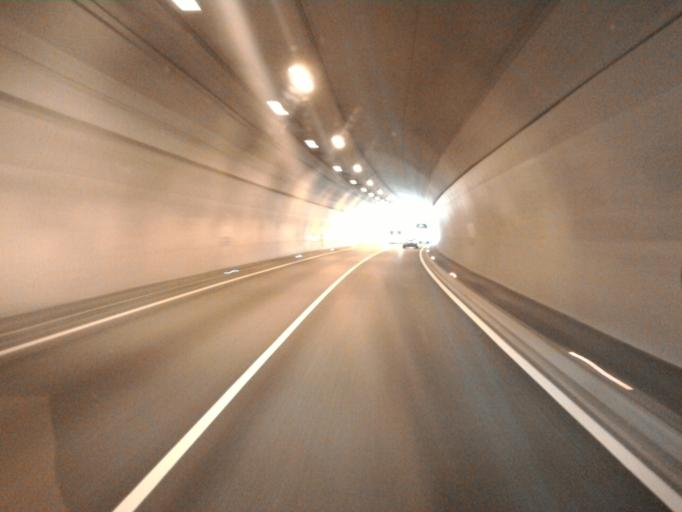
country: AT
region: Tyrol
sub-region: Politischer Bezirk Reutte
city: Heiterwang
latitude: 47.4408
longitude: 10.7472
